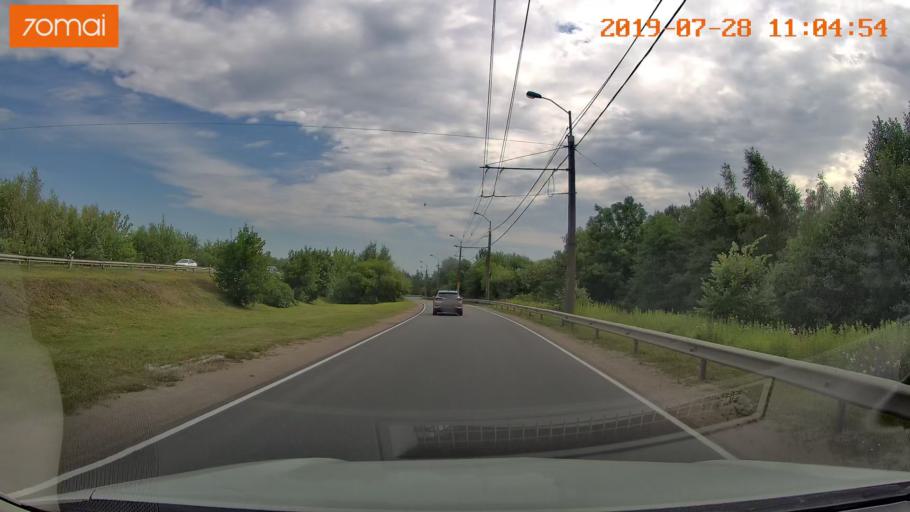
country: RU
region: Kaliningrad
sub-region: Gorod Kaliningrad
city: Kaliningrad
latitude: 54.7179
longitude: 20.3841
